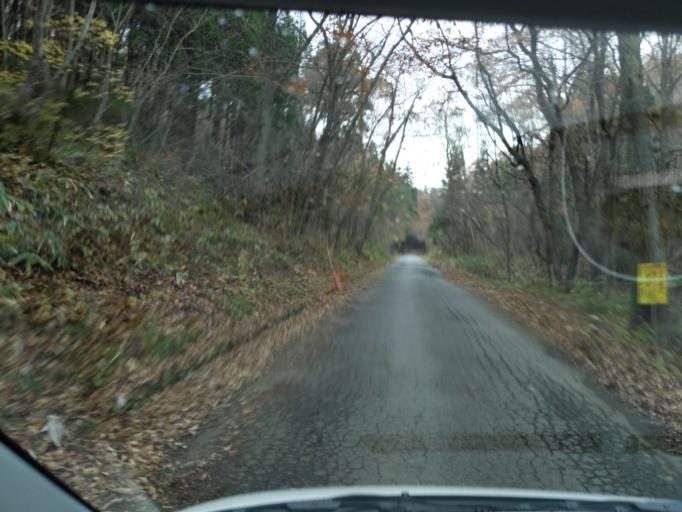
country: JP
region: Iwate
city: Ichinoseki
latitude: 38.9772
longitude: 140.9994
